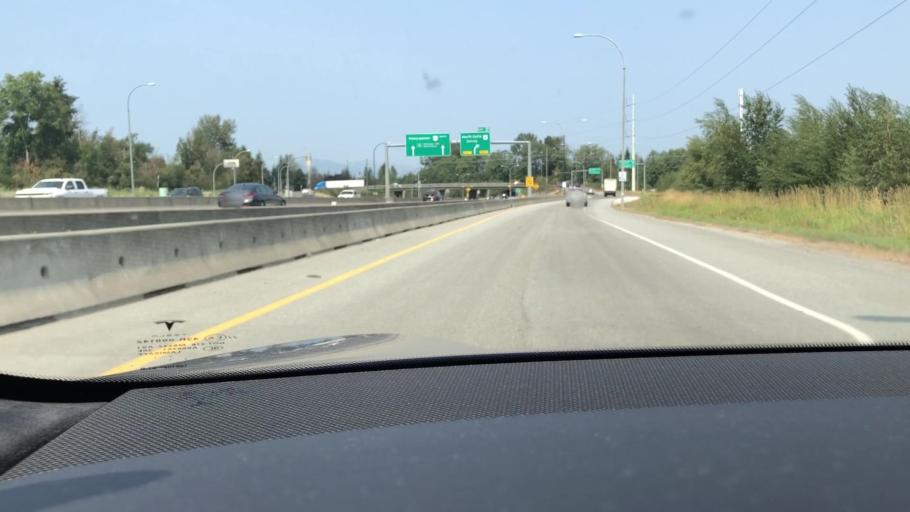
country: CA
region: British Columbia
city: Richmond
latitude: 49.1671
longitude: -123.0863
